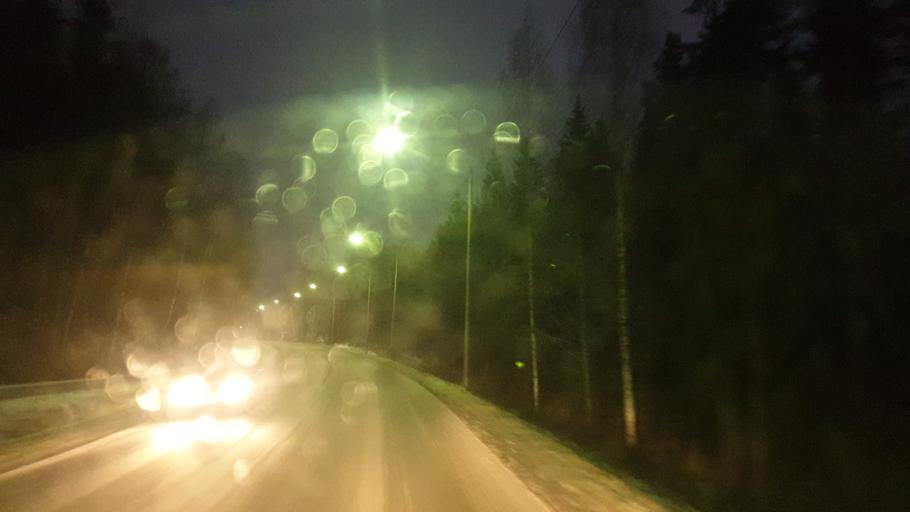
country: FI
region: Southern Savonia
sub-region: Savonlinna
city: Savonlinna
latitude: 61.8617
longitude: 28.9455
